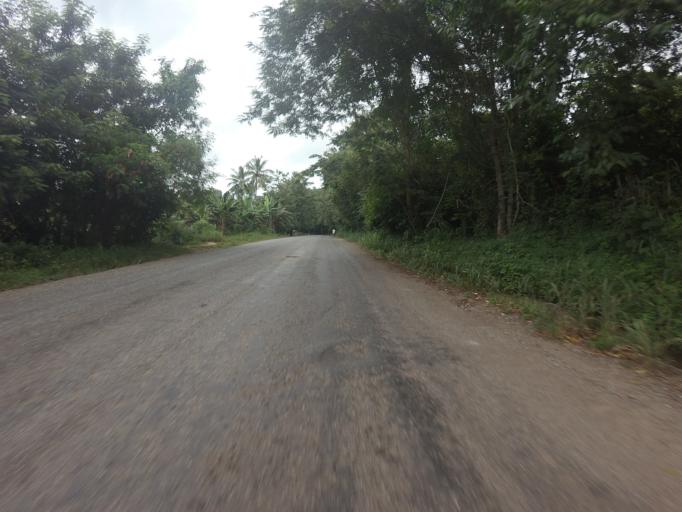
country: GH
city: Akropong
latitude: 5.9584
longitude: -0.1217
